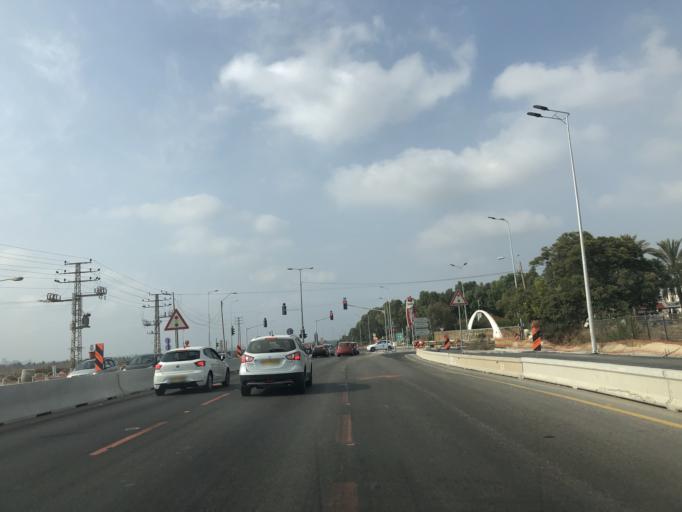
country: IL
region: Central District
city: Rosh Ha'Ayin
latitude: 32.0924
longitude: 34.9412
